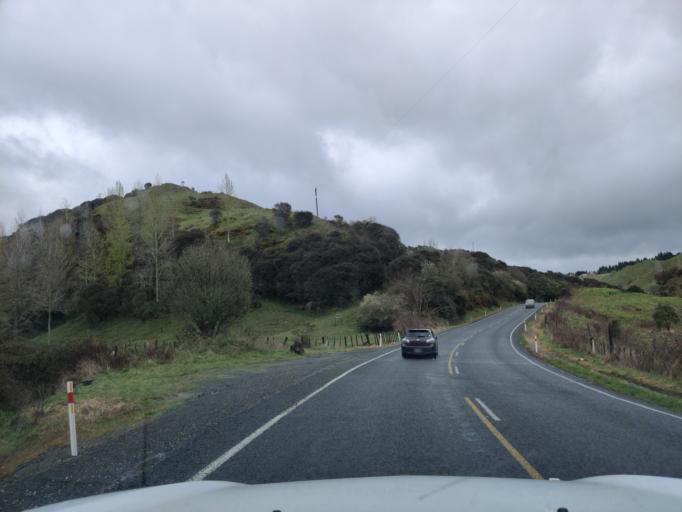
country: NZ
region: Waikato
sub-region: Otorohanga District
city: Otorohanga
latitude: -38.6276
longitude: 175.2127
